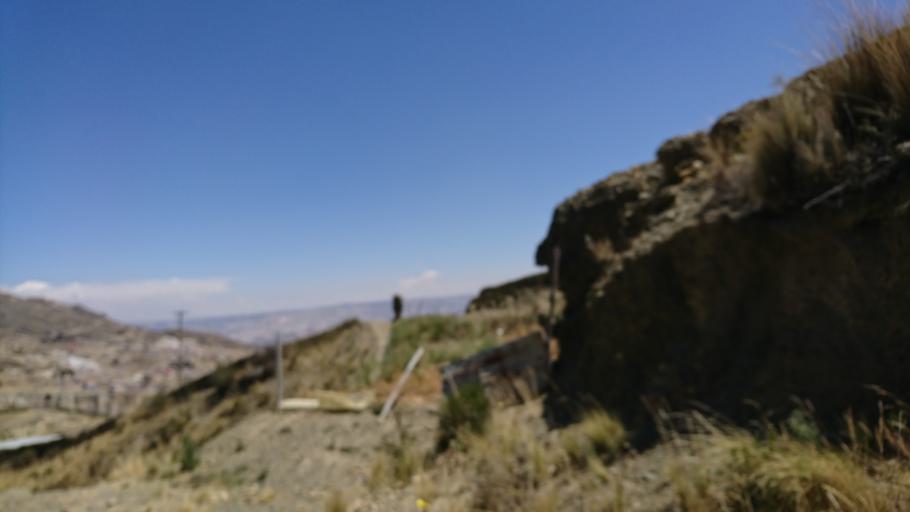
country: BO
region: La Paz
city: La Paz
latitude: -16.5472
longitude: -68.0119
